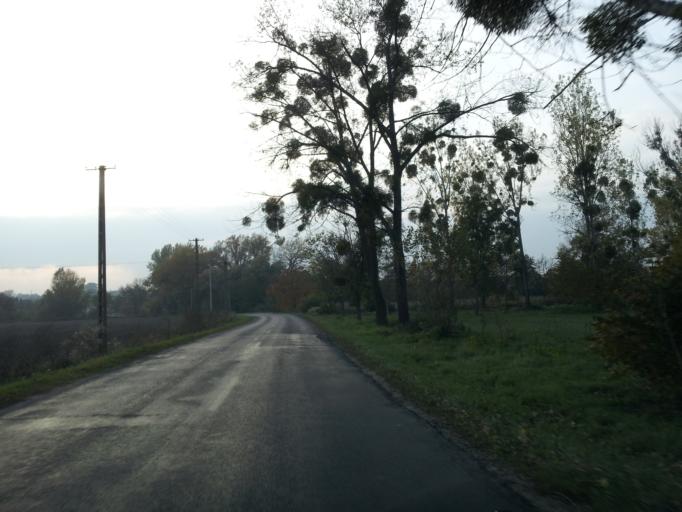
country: HU
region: Komarom-Esztergom
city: Kisber
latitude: 47.4700
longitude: 17.9140
